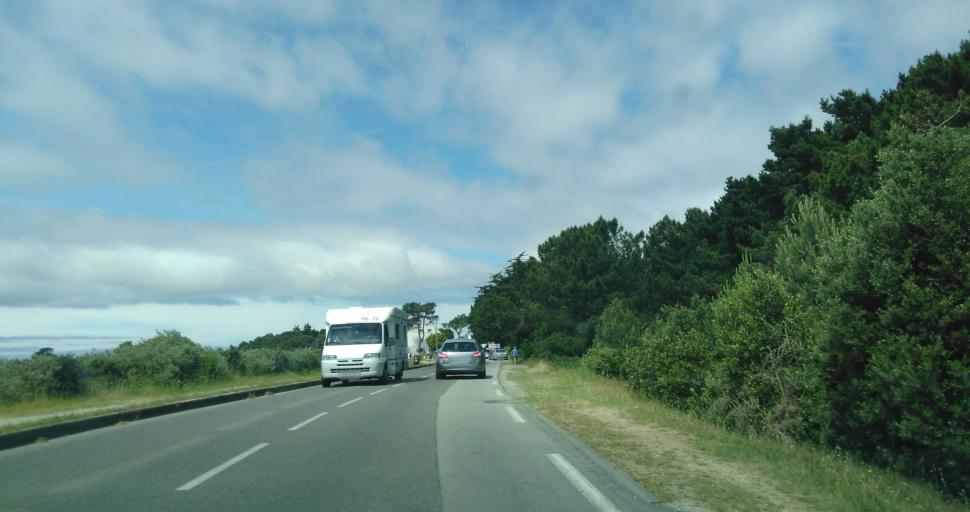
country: FR
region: Brittany
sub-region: Departement du Morbihan
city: La Trinite-sur-Mer
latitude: 47.5787
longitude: -3.0461
